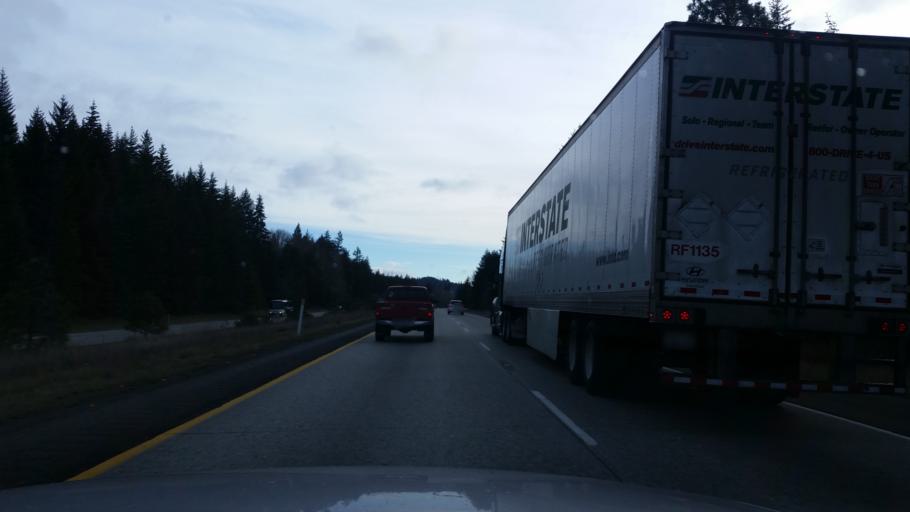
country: US
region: Washington
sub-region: Kittitas County
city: Cle Elum
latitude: 47.2149
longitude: -121.1167
